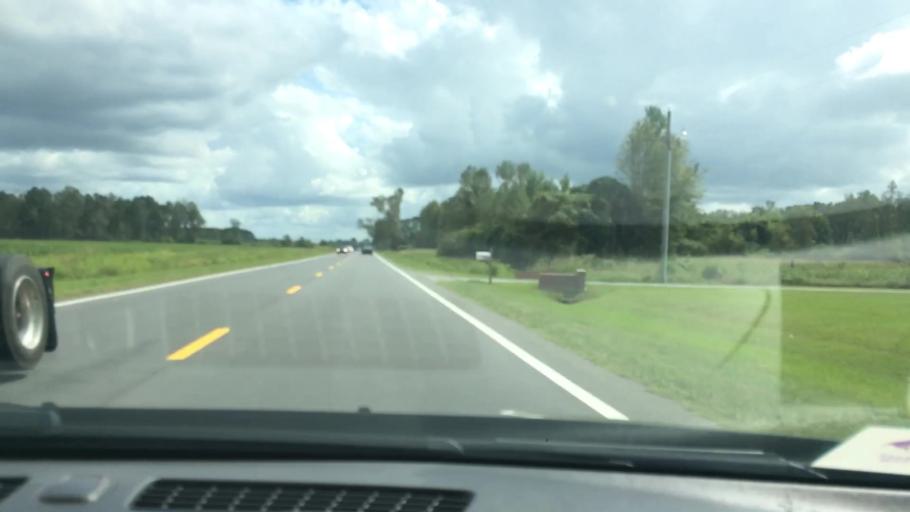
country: US
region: North Carolina
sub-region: Pitt County
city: Farmville
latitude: 35.5581
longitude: -77.5577
